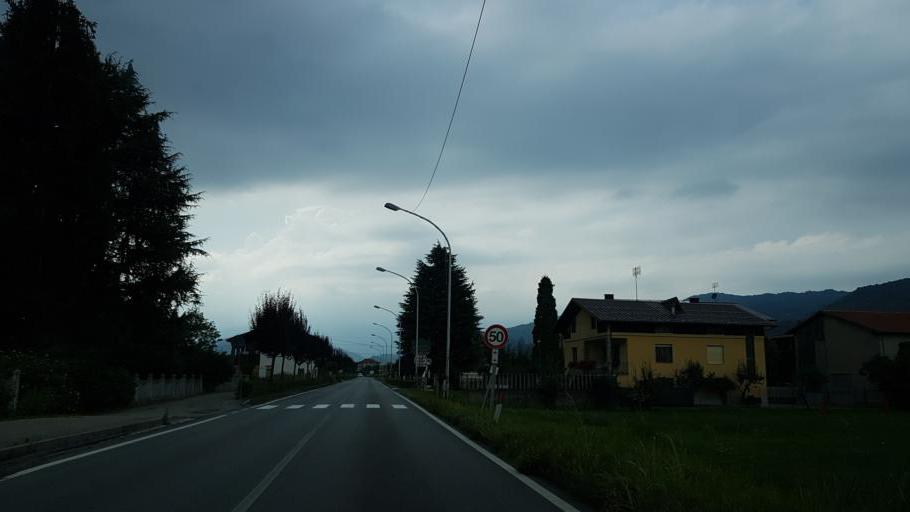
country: IT
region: Piedmont
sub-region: Provincia di Cuneo
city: Roccavione
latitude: 44.3330
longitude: 7.4720
